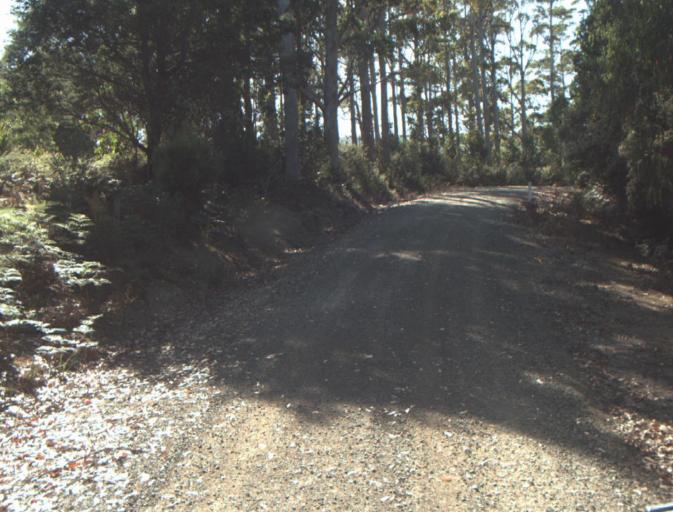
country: AU
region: Tasmania
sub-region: Dorset
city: Scottsdale
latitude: -41.2735
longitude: 147.3737
